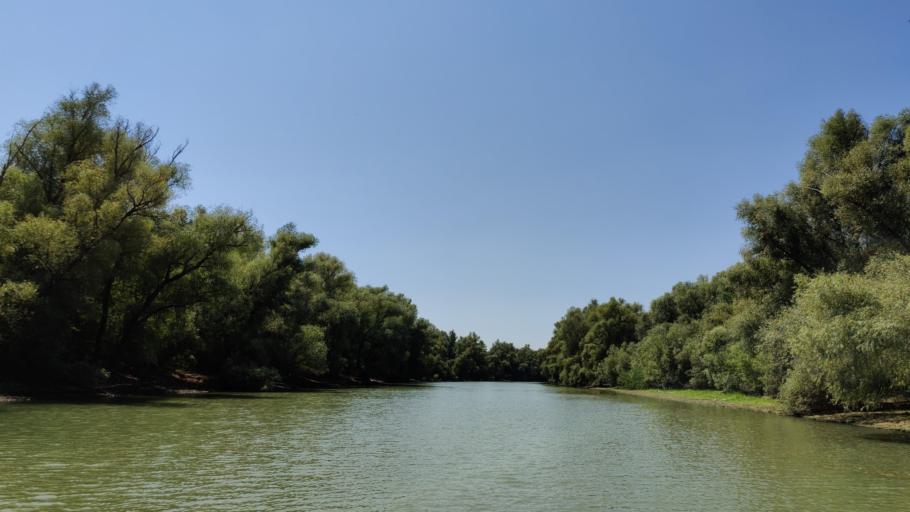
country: RO
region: Tulcea
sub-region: Comuna Pardina
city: Pardina
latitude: 45.2345
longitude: 28.9134
